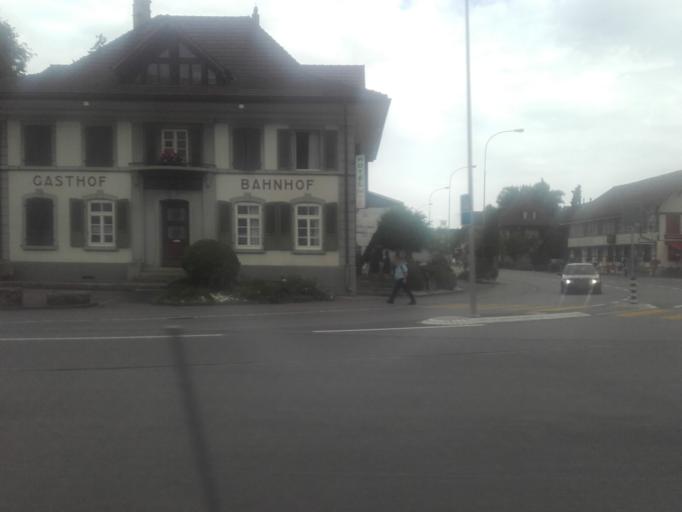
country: CH
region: Bern
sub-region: Emmental District
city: Utzenstorf
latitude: 47.1307
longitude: 7.5536
